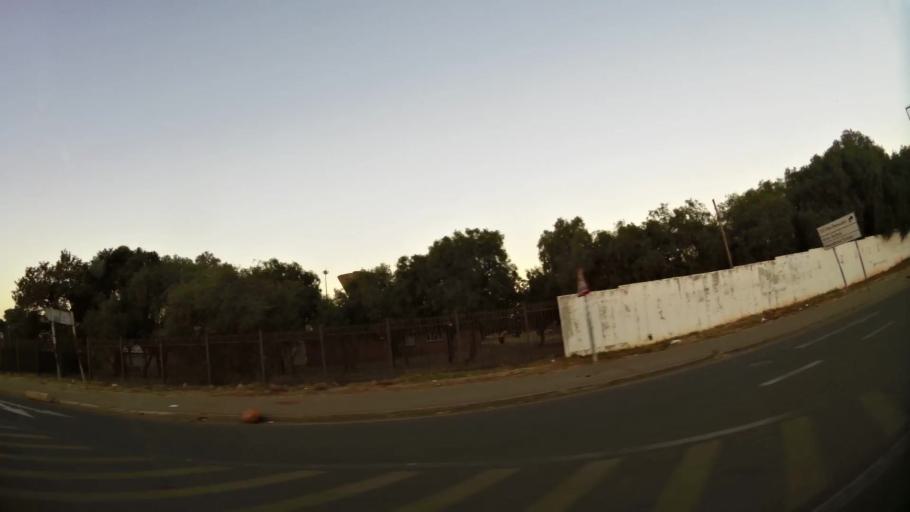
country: ZA
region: North-West
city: Ga-Rankuwa
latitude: -25.6185
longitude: 28.0071
